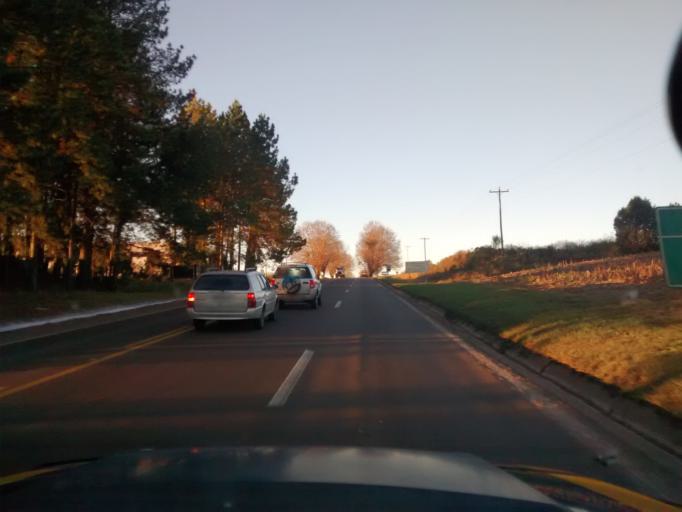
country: BR
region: Rio Grande do Sul
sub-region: Vacaria
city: Vacaria
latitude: -28.5262
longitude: -50.9480
